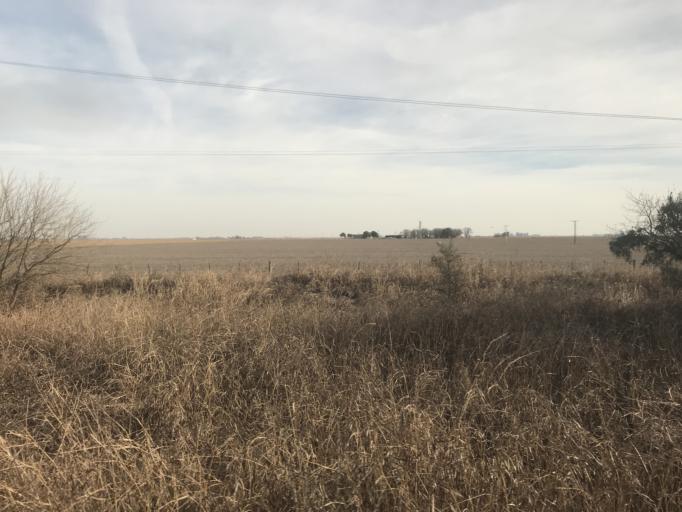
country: AR
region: Cordoba
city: Pilar
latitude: -31.7166
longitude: -63.8557
